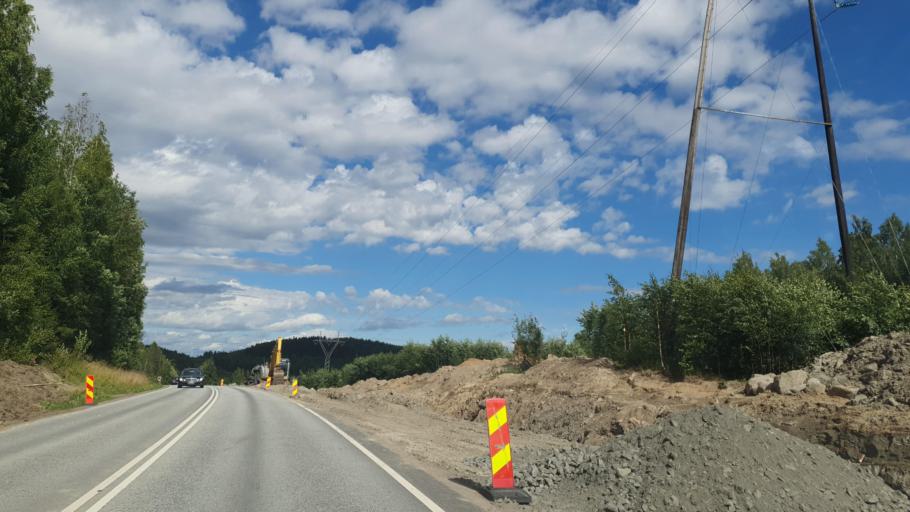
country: FI
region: Central Finland
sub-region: Jyvaeskylae
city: Muurame
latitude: 62.1412
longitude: 25.7000
